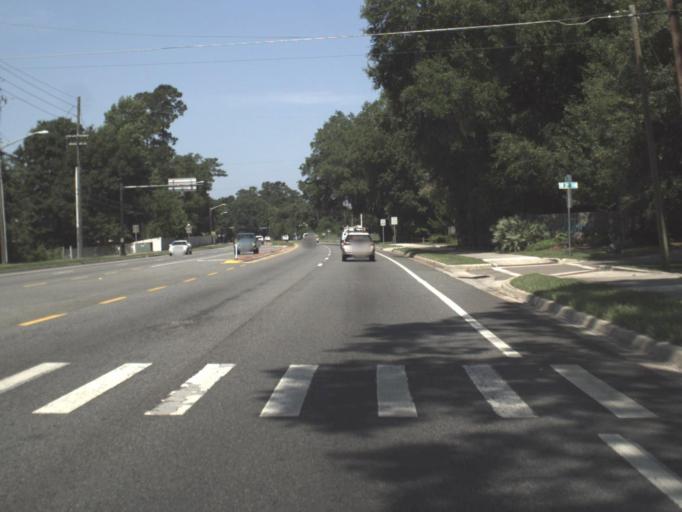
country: US
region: Florida
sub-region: Alachua County
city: Gainesville
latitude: 29.6142
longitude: -82.3512
